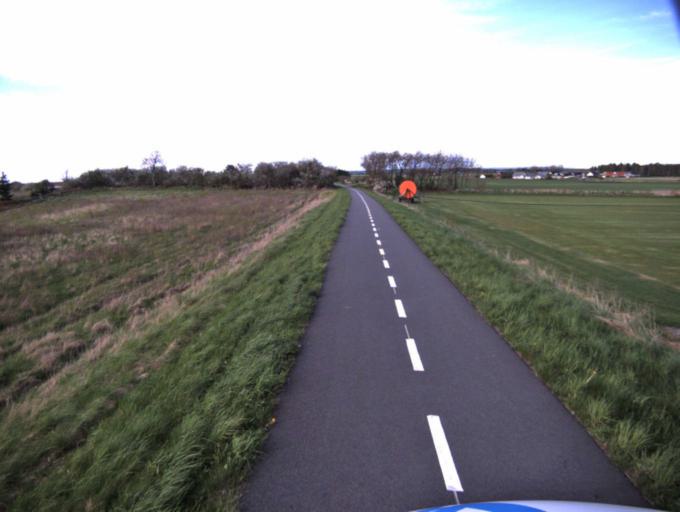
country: SE
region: Skane
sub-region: Kristianstads Kommun
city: Kristianstad
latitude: 56.0120
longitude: 14.0826
